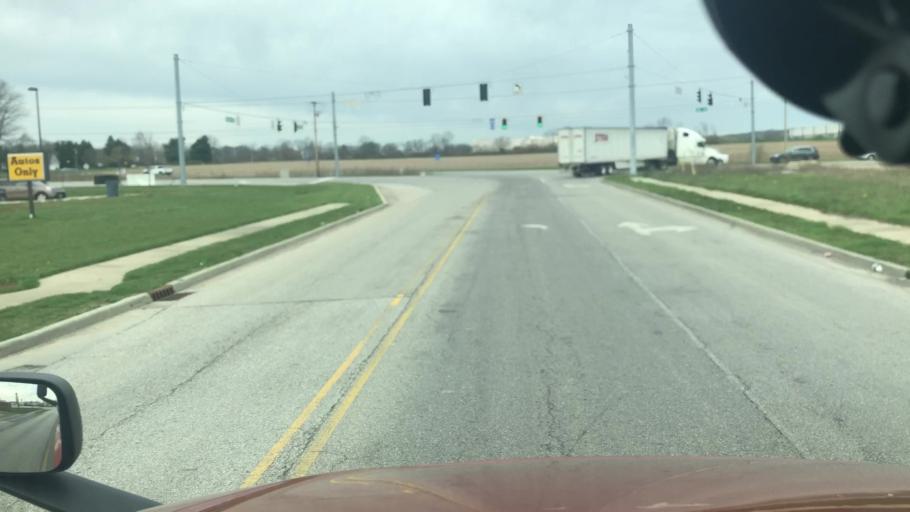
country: US
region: Indiana
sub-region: Morgan County
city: Monrovia
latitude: 39.6167
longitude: -86.4788
